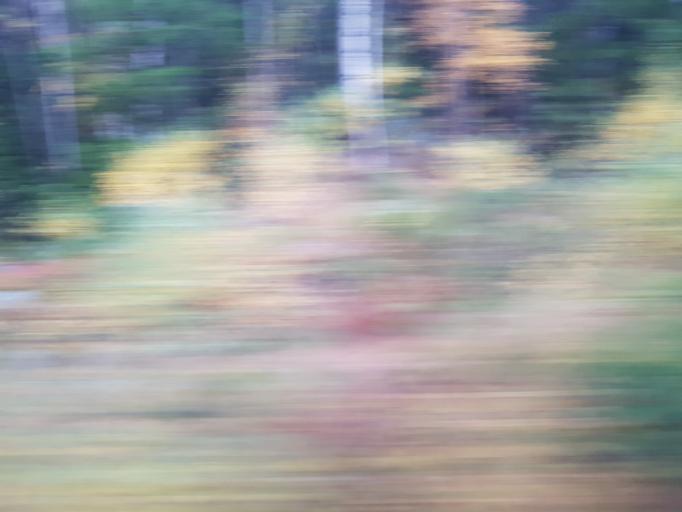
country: NO
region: Oppland
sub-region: Sel
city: Otta
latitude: 61.8579
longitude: 9.4139
